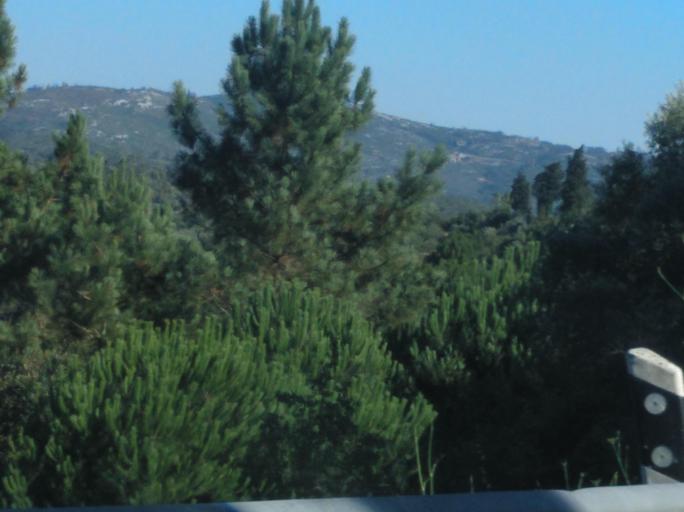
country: PT
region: Leiria
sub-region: Porto de Mos
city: Porto de Mos
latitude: 39.5839
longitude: -8.8087
